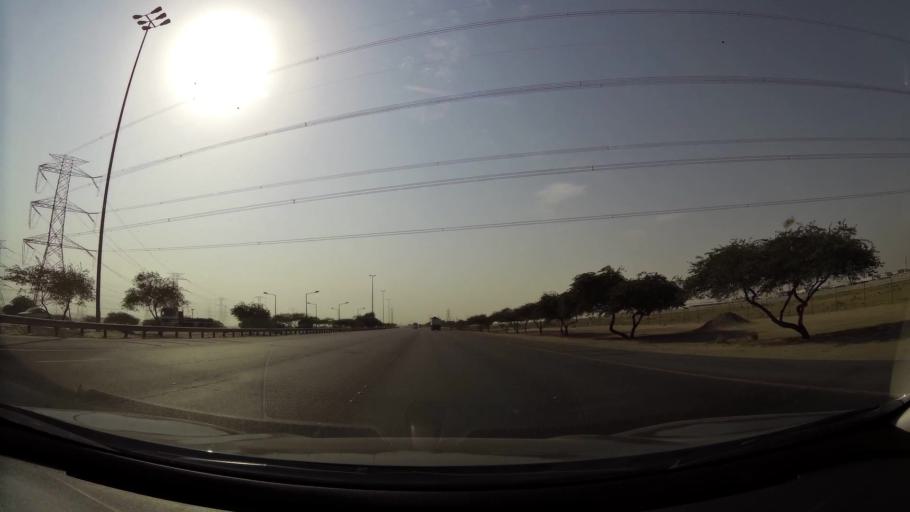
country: KW
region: Al Ahmadi
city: Al Ahmadi
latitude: 29.0025
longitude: 48.0961
